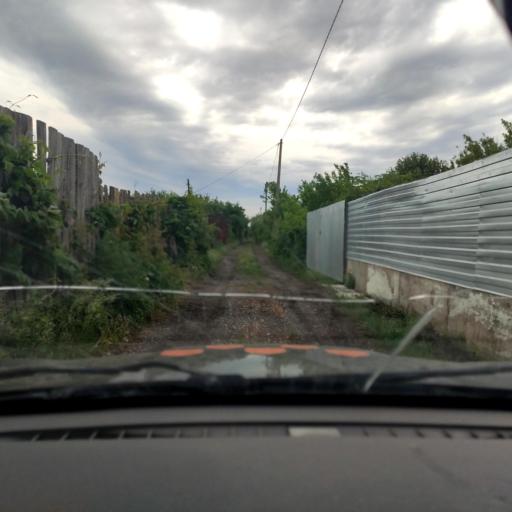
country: RU
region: Samara
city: Tol'yatti
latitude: 53.5898
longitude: 49.4404
